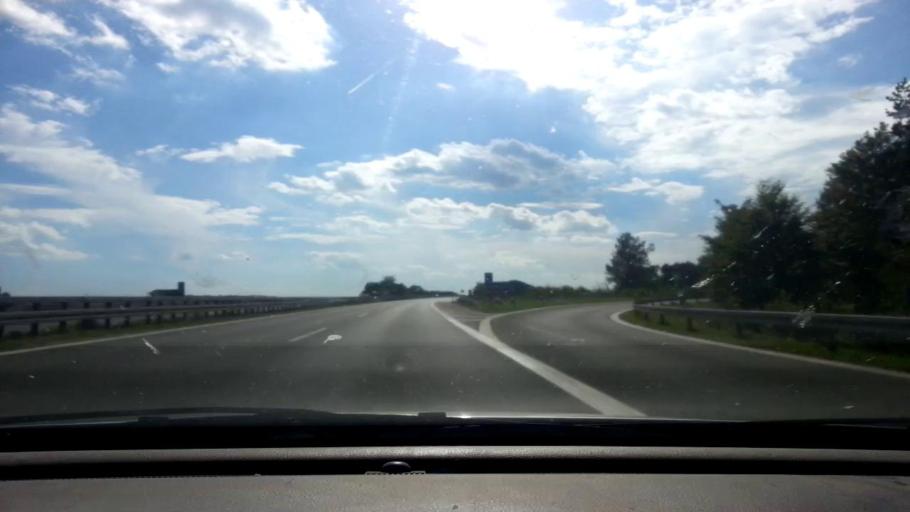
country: DE
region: Bavaria
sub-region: Upper Franconia
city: Stadelhofen
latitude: 50.0014
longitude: 11.2117
